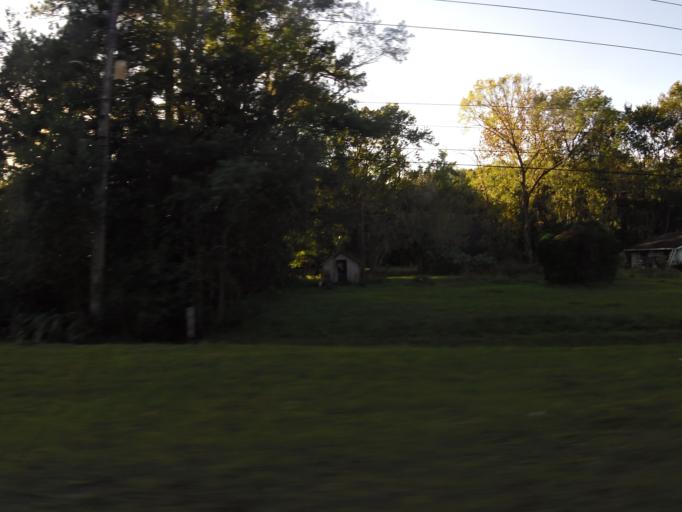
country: US
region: Florida
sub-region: Duval County
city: Jacksonville
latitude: 30.3247
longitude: -81.7710
